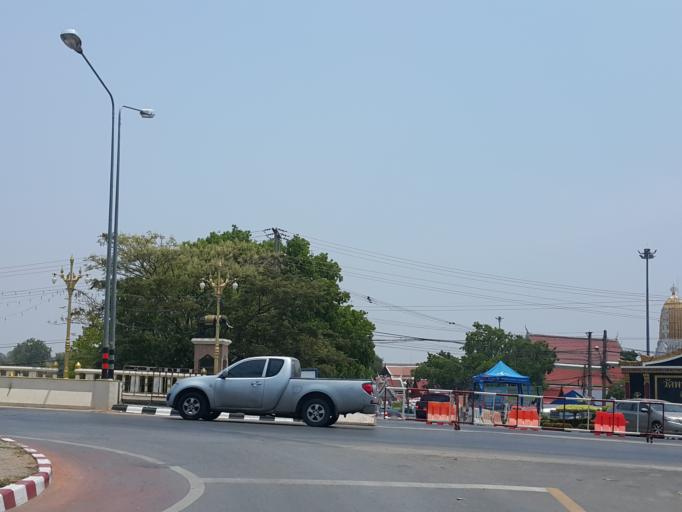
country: TH
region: Phitsanulok
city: Phitsanulok
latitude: 16.8224
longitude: 100.2607
